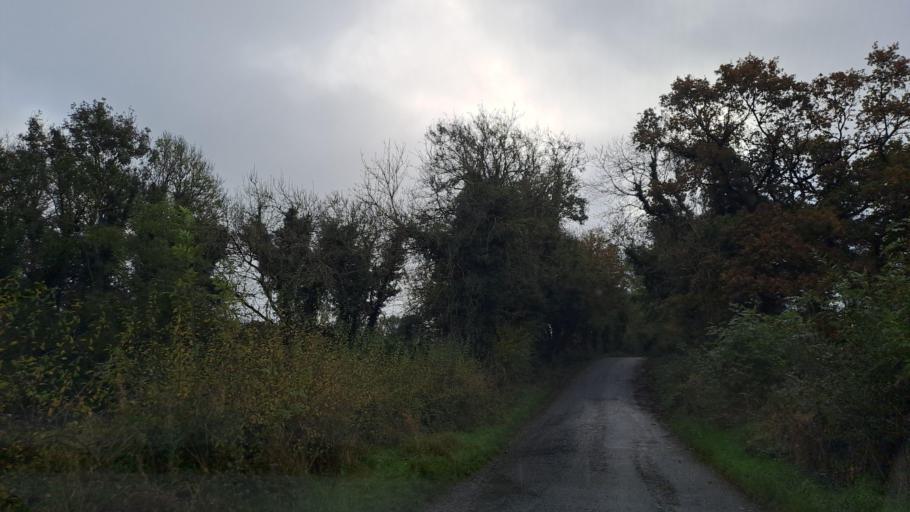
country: IE
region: Ulster
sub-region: An Cabhan
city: Bailieborough
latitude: 53.9731
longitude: -6.9898
